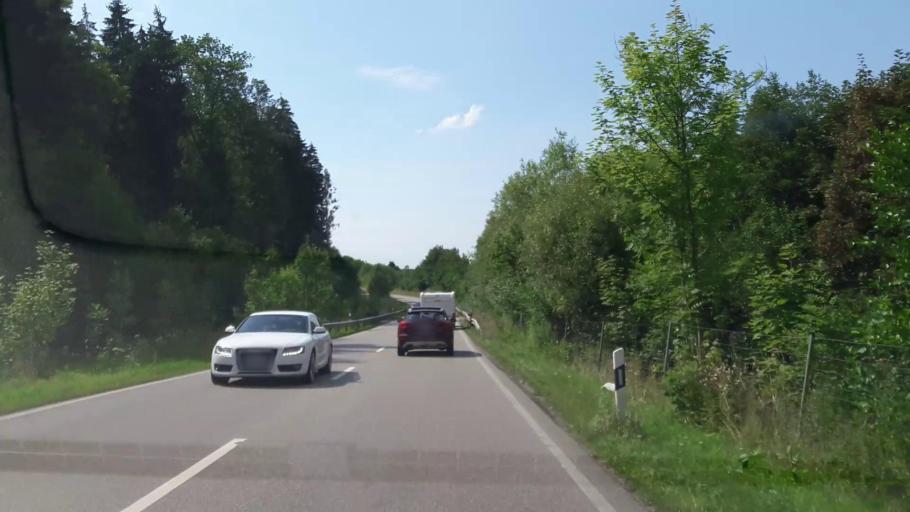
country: DE
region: Bavaria
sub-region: Upper Bavaria
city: Teisendorf
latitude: 47.8407
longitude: 12.8246
